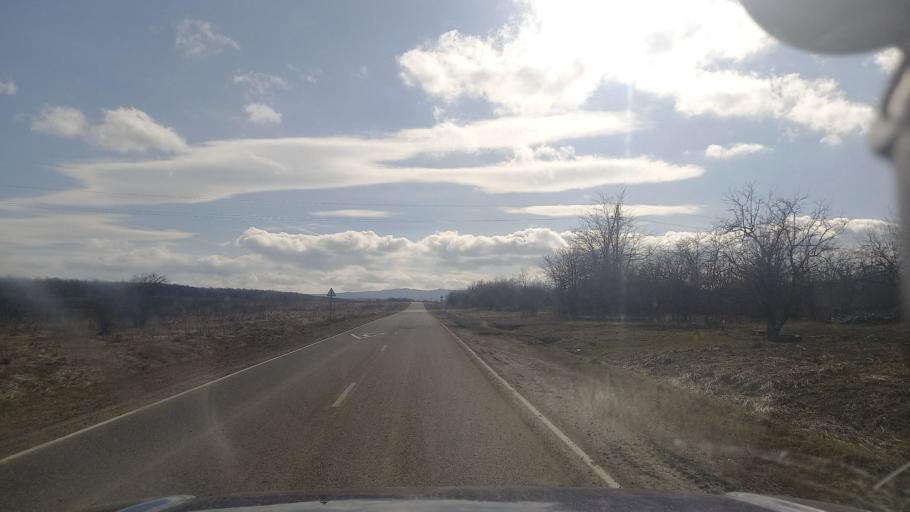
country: RU
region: Krasnodarskiy
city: Novodmitriyevskaya
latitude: 44.7525
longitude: 38.9961
